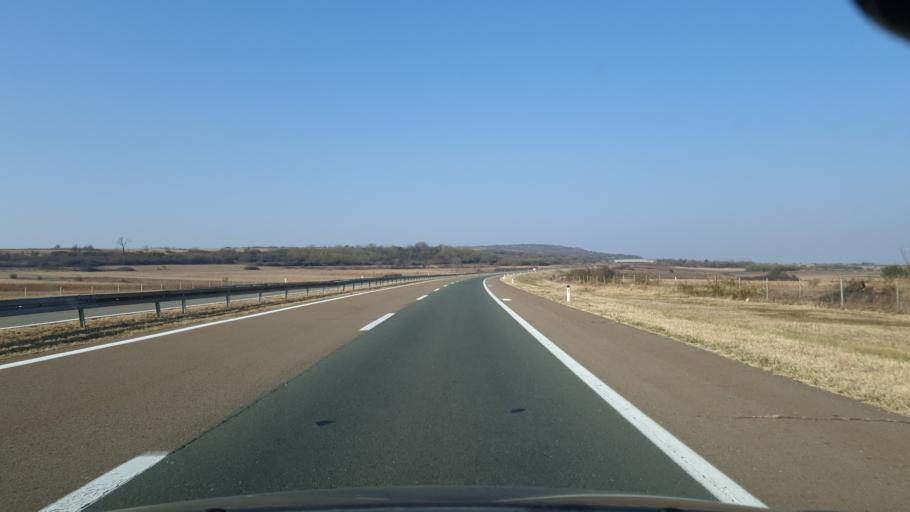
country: RS
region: Central Serbia
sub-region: Nisavski Okrug
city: Doljevac
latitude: 43.2351
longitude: 21.8217
